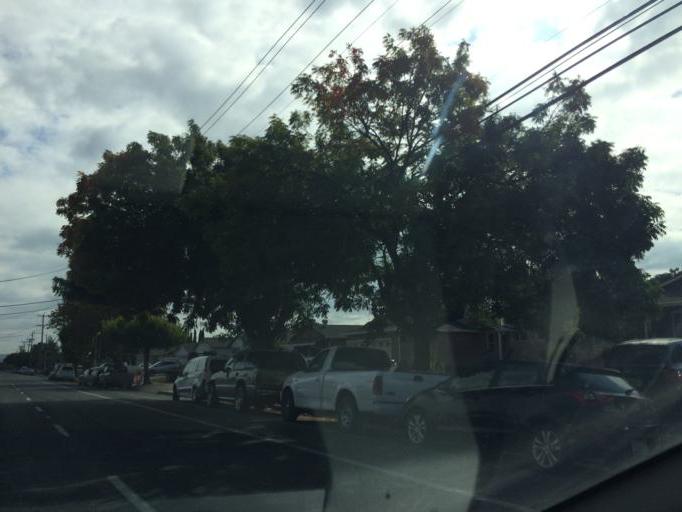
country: US
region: California
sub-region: Santa Clara County
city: Alum Rock
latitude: 37.3734
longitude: -121.8343
